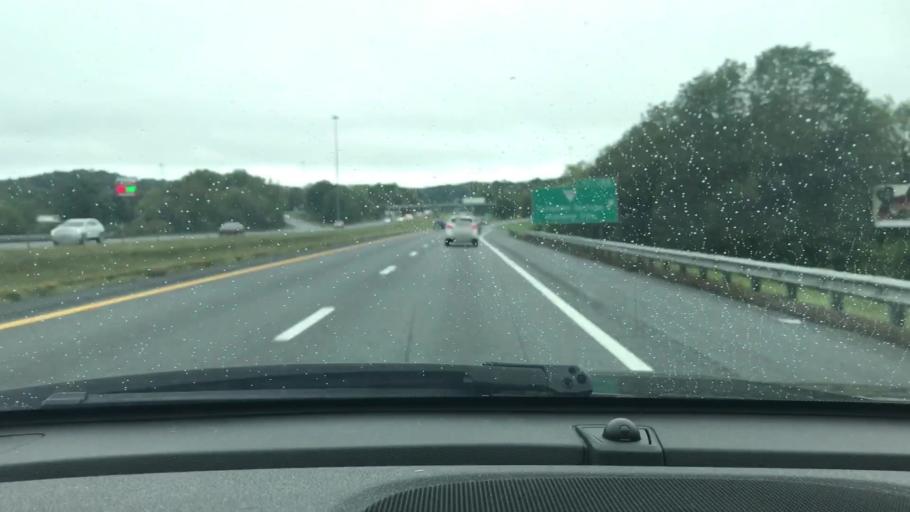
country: US
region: Tennessee
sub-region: Cheatham County
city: Kingston Springs
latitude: 36.0847
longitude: -87.0925
